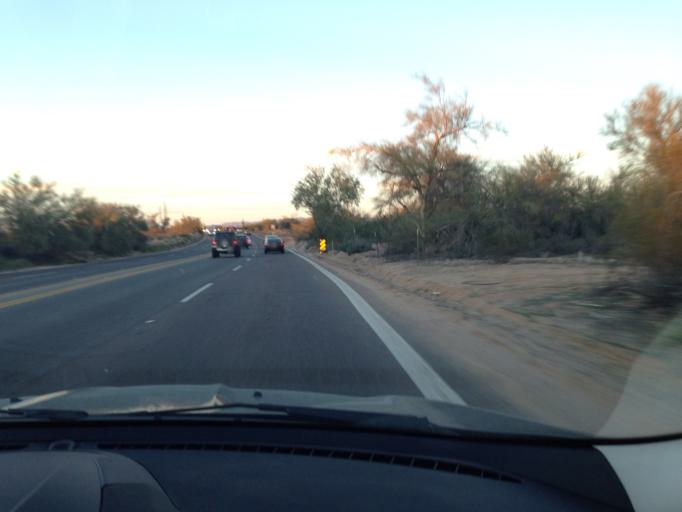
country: US
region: Arizona
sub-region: Maricopa County
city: Carefree
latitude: 33.7014
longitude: -111.9688
